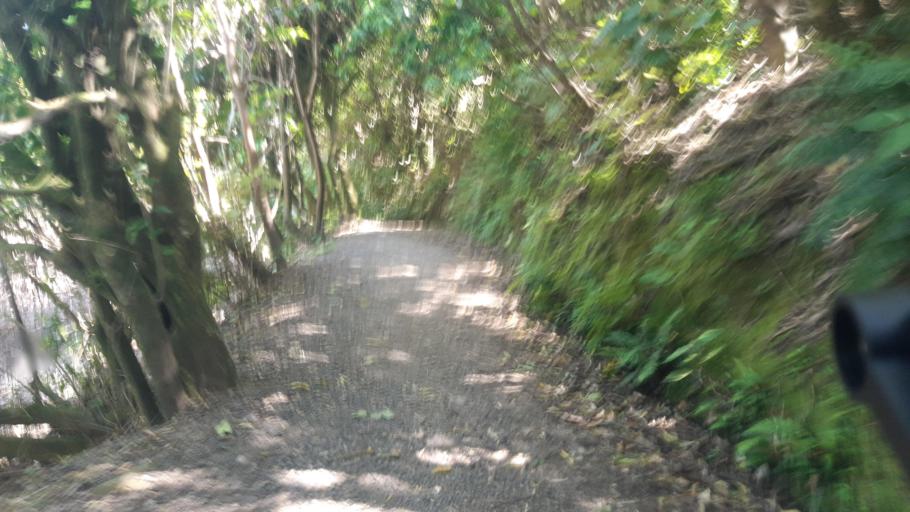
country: NZ
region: Marlborough
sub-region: Marlborough District
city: Picton
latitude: -41.2694
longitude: 174.0326
